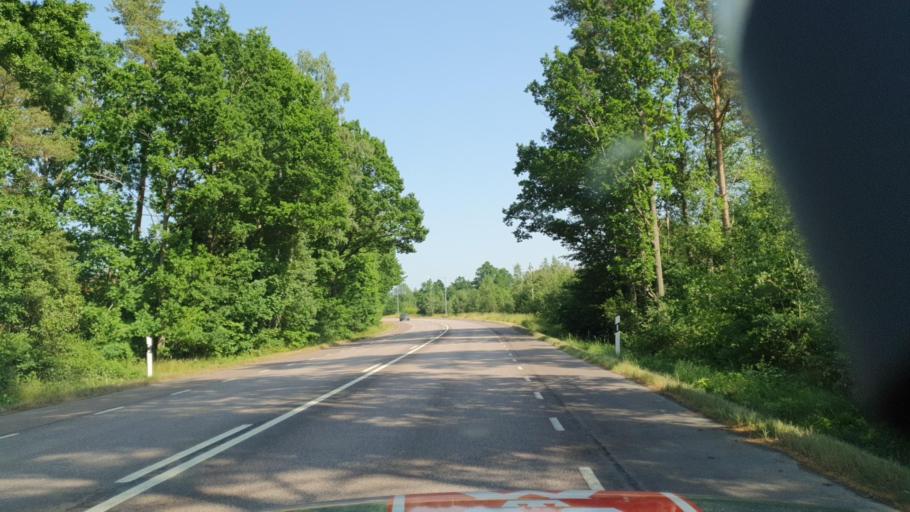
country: SE
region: Kalmar
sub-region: Nybro Kommun
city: Nybro
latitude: 56.7531
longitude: 15.8883
